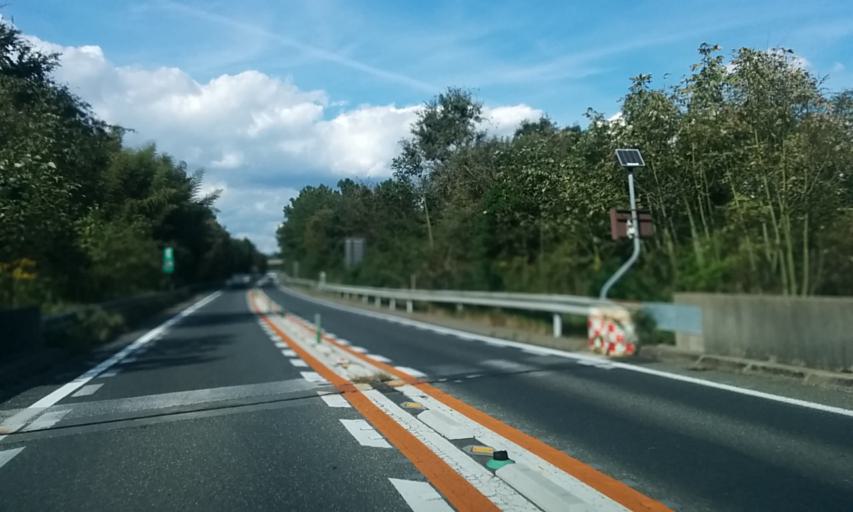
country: JP
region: Kyoto
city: Tanabe
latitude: 34.8192
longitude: 135.7513
